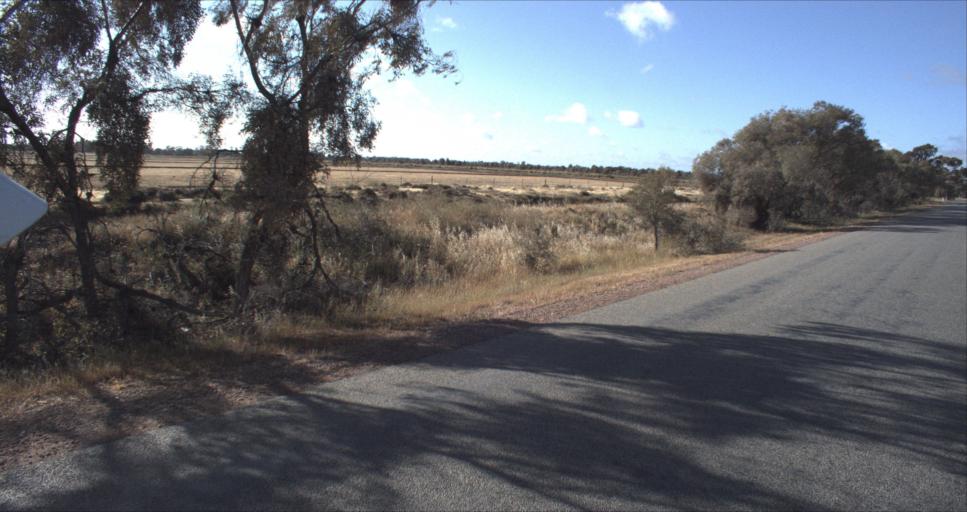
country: AU
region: New South Wales
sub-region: Leeton
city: Leeton
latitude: -34.5147
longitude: 146.3917
